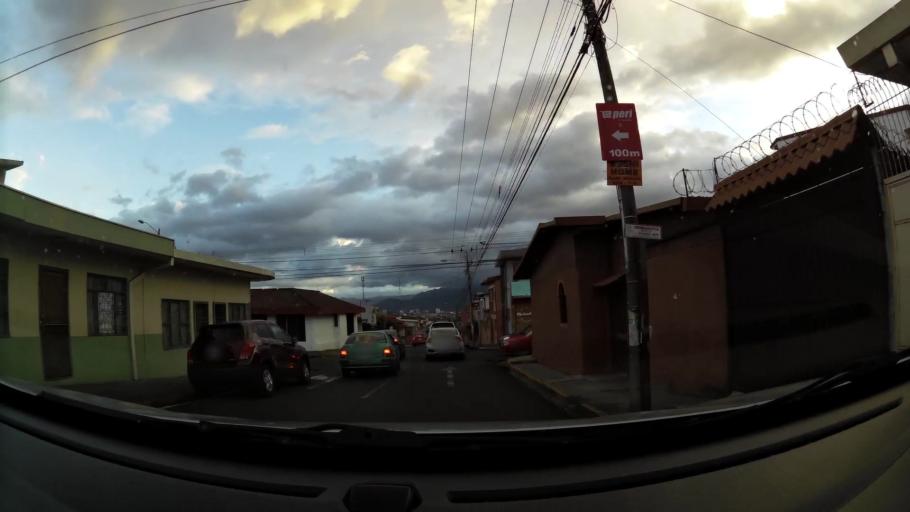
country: CR
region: Heredia
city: Heredia
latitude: 10.0014
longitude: -84.1134
